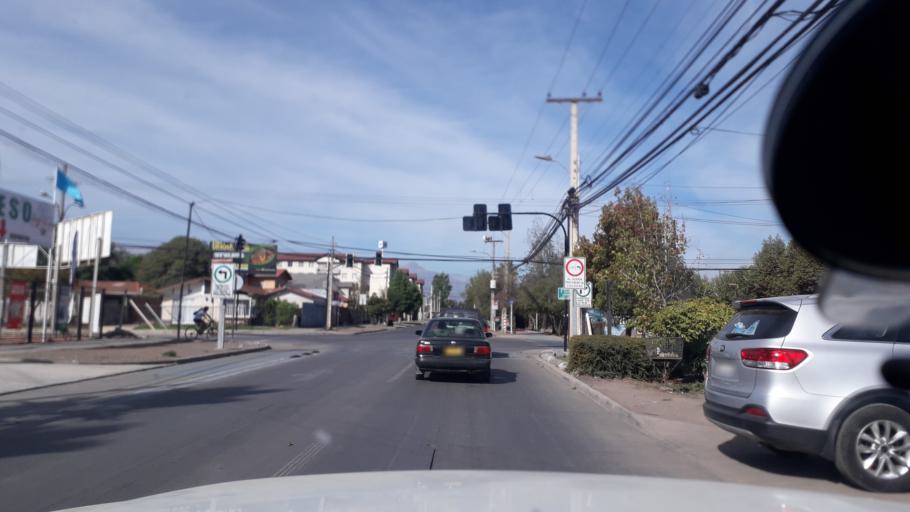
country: CL
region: Valparaiso
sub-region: Provincia de San Felipe
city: San Felipe
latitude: -32.7533
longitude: -70.7123
